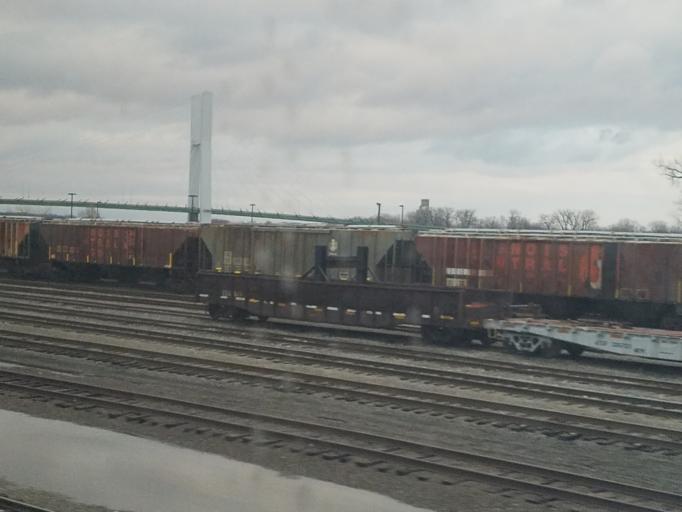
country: US
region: Iowa
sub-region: Des Moines County
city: Burlington
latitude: 40.8052
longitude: -91.1008
